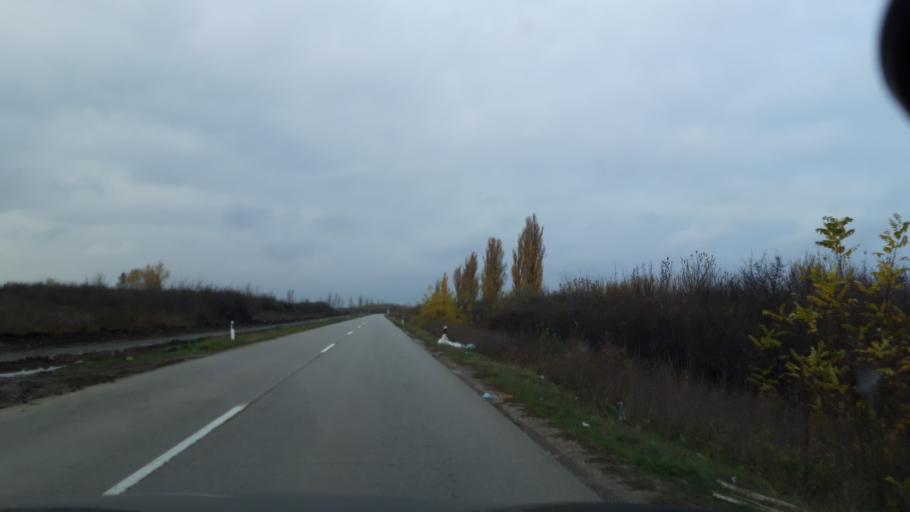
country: RS
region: Autonomna Pokrajina Vojvodina
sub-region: Severnobanatski Okrug
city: Novi Knezevac
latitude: 46.0721
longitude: 20.1033
